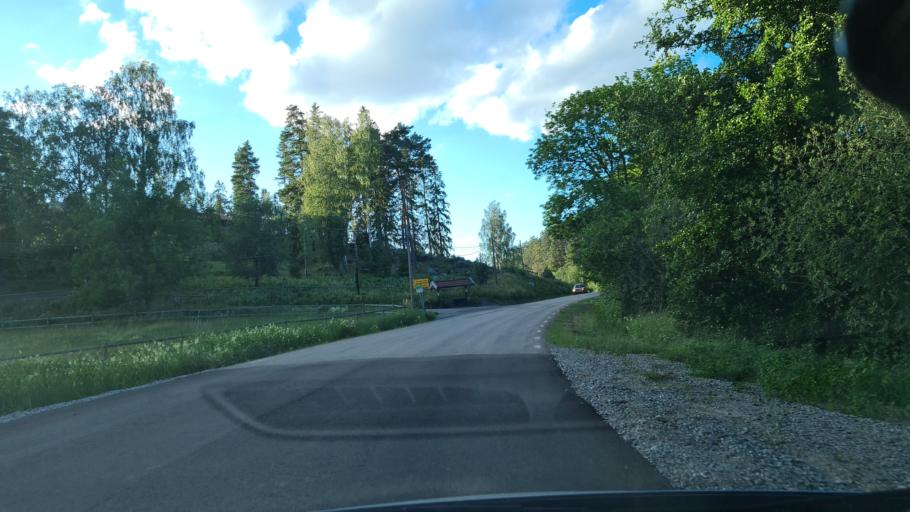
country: SE
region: Soedermanland
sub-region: Gnesta Kommun
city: Gnesta
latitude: 59.0279
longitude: 17.3353
